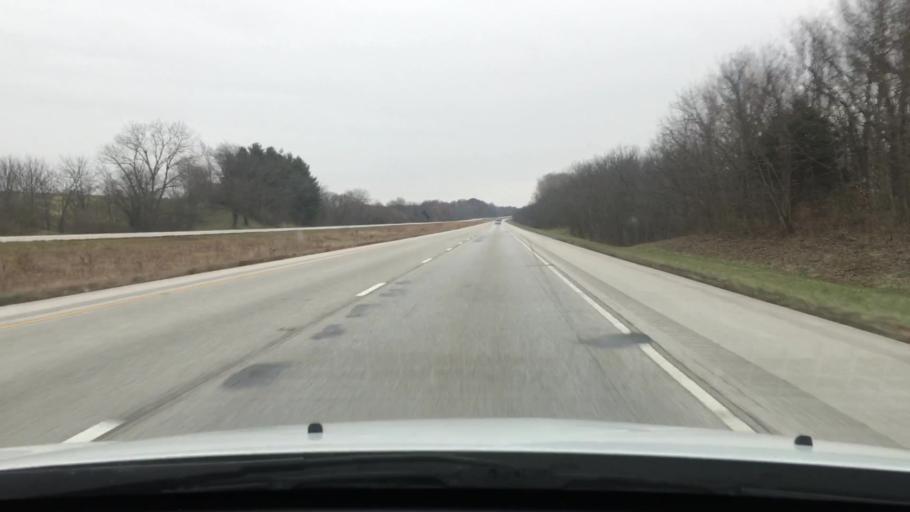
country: US
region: Illinois
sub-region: Scott County
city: Winchester
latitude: 39.6812
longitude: -90.4084
